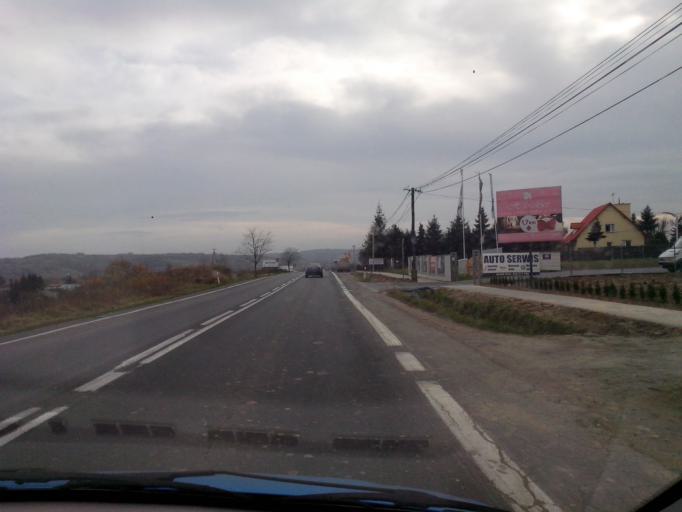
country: PL
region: Subcarpathian Voivodeship
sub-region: Powiat rzeszowski
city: Lutoryz
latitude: 49.9689
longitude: 21.9215
